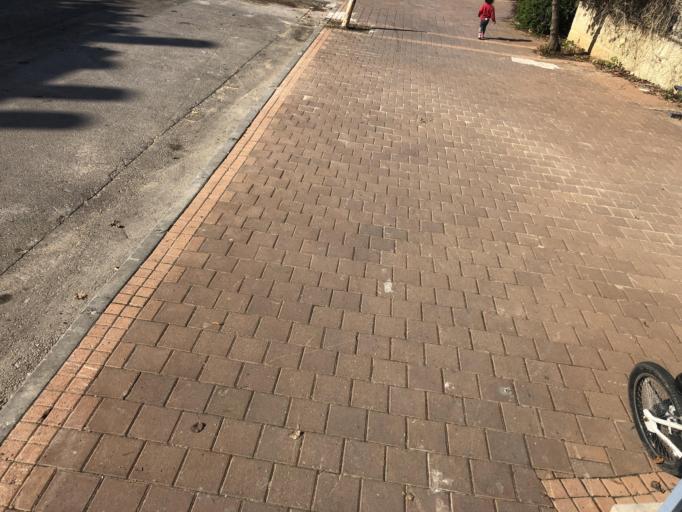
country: IL
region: Jerusalem
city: Modiin Ilit
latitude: 31.9230
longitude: 35.0473
